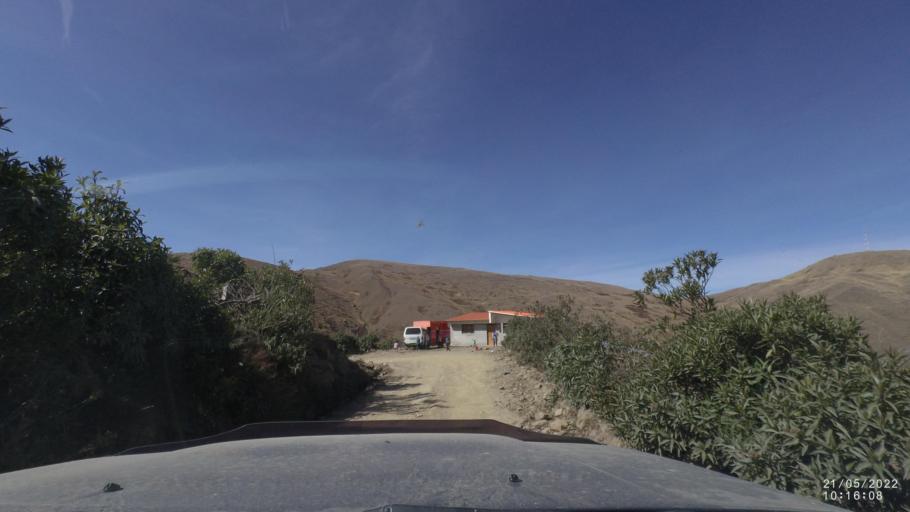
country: BO
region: Cochabamba
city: Colomi
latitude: -17.3324
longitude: -65.9673
